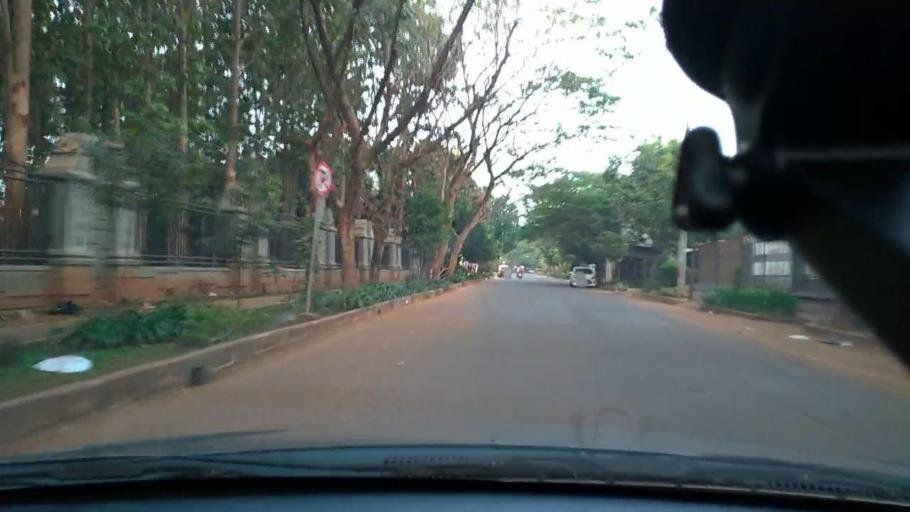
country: ID
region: West Java
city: Purwakarta
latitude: -6.5321
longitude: 107.4397
